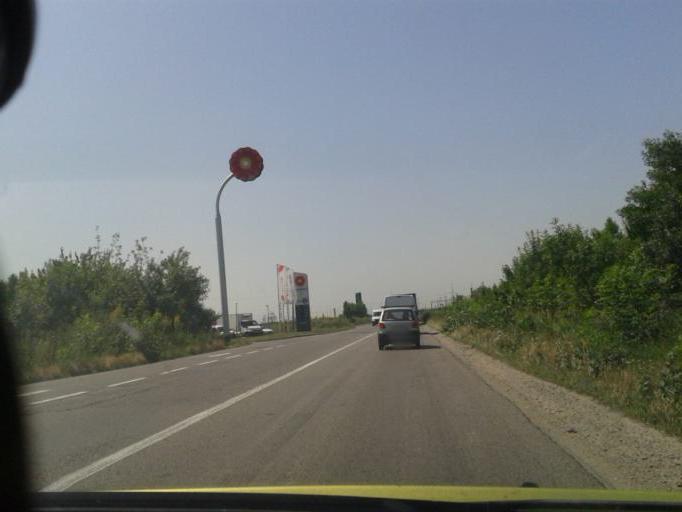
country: RO
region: Ilfov
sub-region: Comuna Glina
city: Catelu
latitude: 44.4134
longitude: 26.2357
